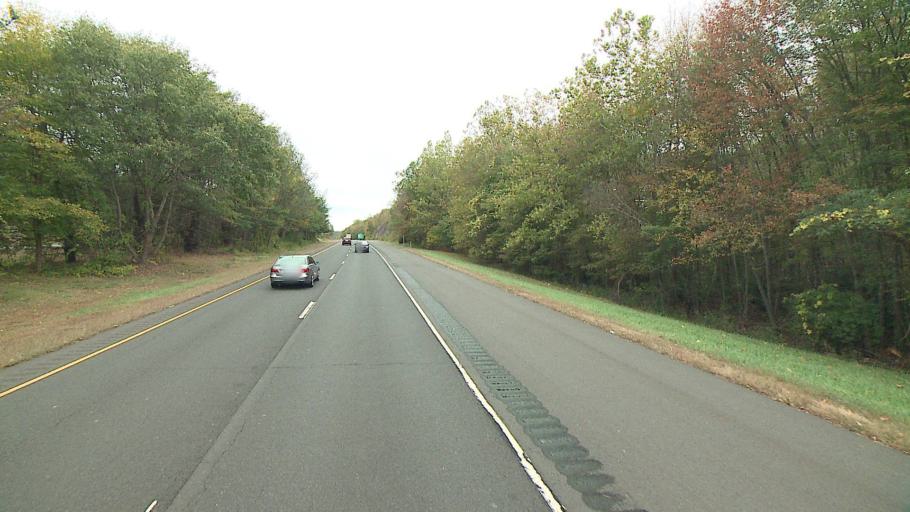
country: US
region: Connecticut
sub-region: Middlesex County
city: Higganum
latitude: 41.4896
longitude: -72.5668
